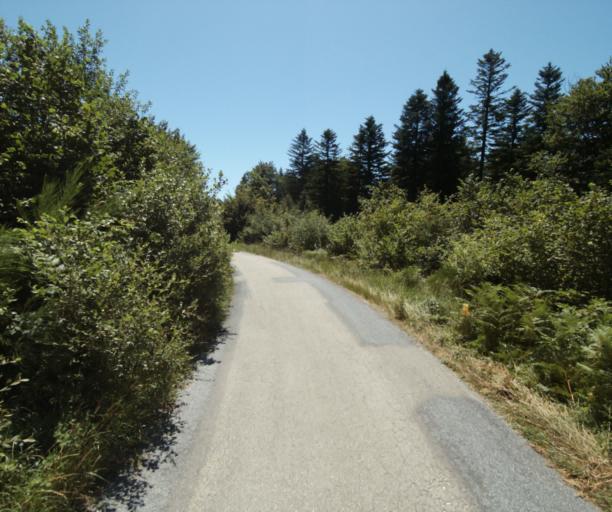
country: FR
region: Languedoc-Roussillon
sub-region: Departement de l'Aude
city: Cuxac-Cabardes
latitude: 43.4088
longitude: 2.1999
